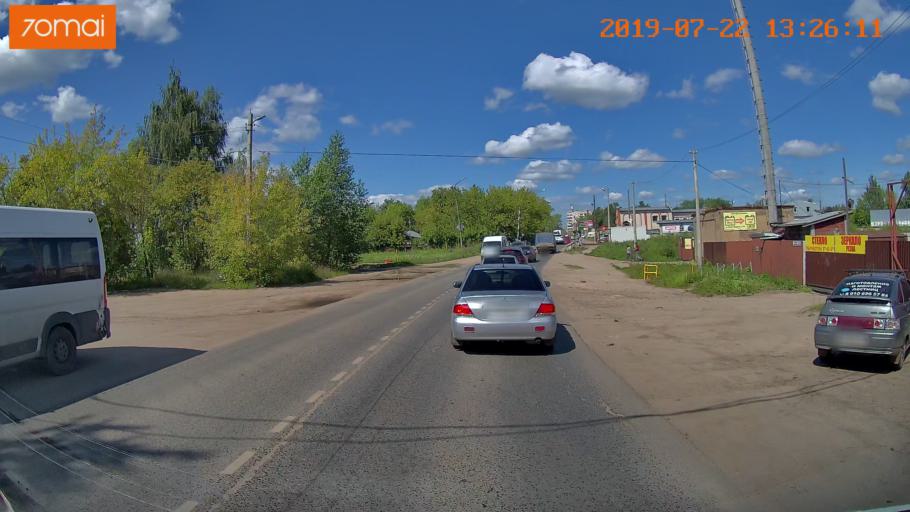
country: RU
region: Ivanovo
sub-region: Gorod Ivanovo
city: Ivanovo
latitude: 57.0284
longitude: 40.9483
